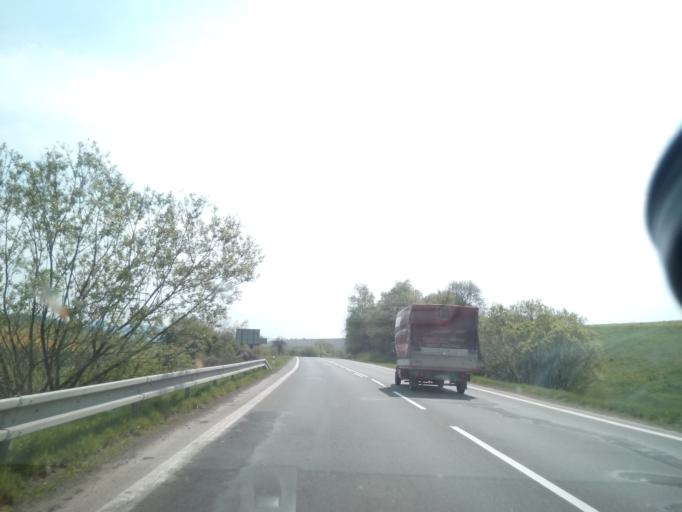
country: SK
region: Presovsky
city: Giraltovce
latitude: 49.0329
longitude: 21.4724
